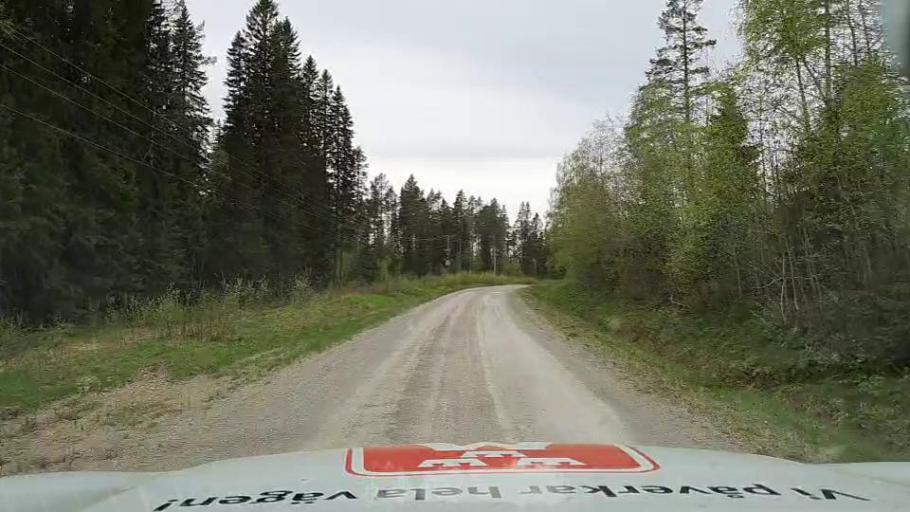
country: SE
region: Jaemtland
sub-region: Bergs Kommun
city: Hoverberg
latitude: 62.6705
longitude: 14.8076
